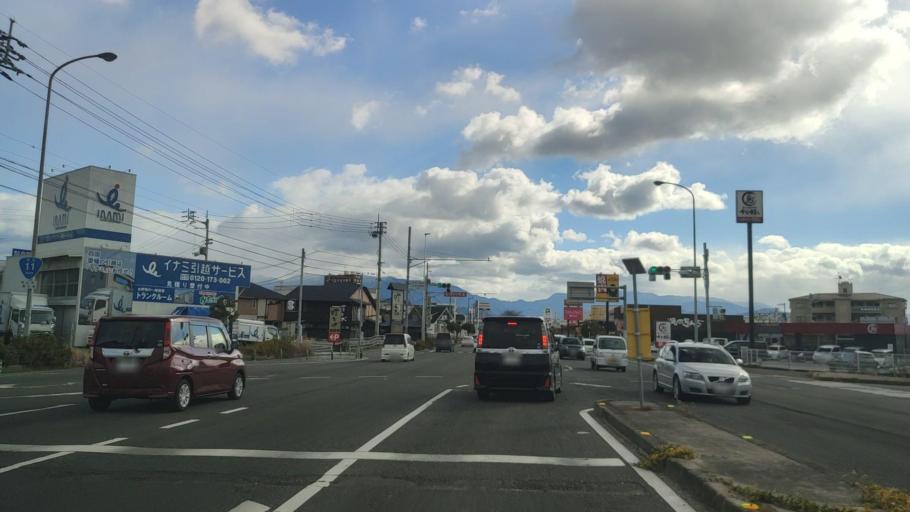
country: JP
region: Ehime
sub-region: Shikoku-chuo Shi
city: Matsuyama
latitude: 33.8146
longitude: 132.7954
